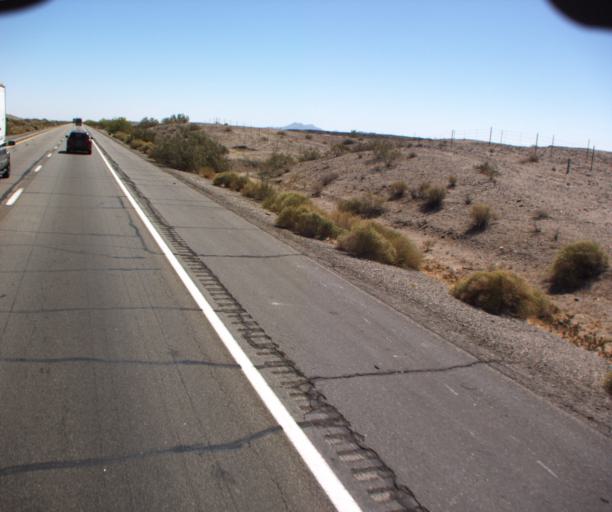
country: US
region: Arizona
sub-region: Yuma County
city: Wellton
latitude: 32.6573
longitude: -114.2445
